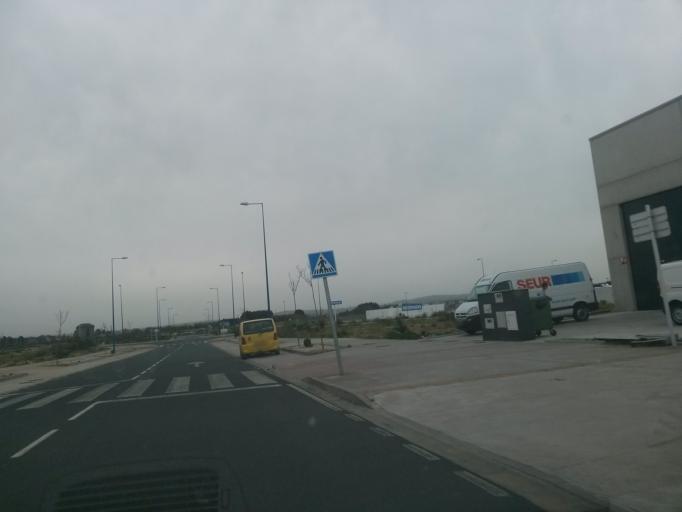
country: ES
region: Galicia
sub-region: Provincia de Lugo
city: Lugo
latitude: 43.0409
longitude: -7.5500
